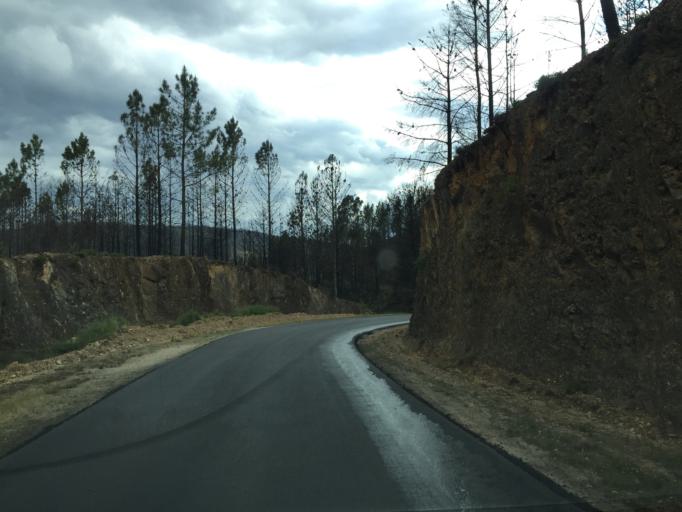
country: PT
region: Coimbra
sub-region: Pampilhosa da Serra
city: Pampilhosa da Serra
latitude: 40.0577
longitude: -8.0139
